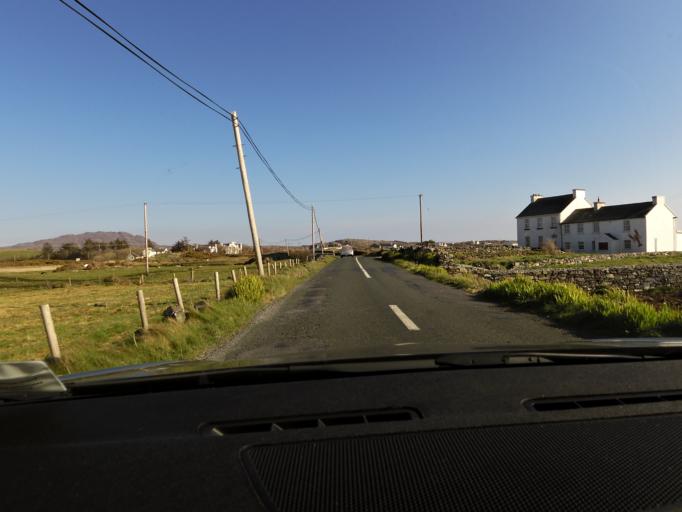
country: IE
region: Connaught
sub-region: County Galway
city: Clifden
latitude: 53.4105
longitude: -10.0379
